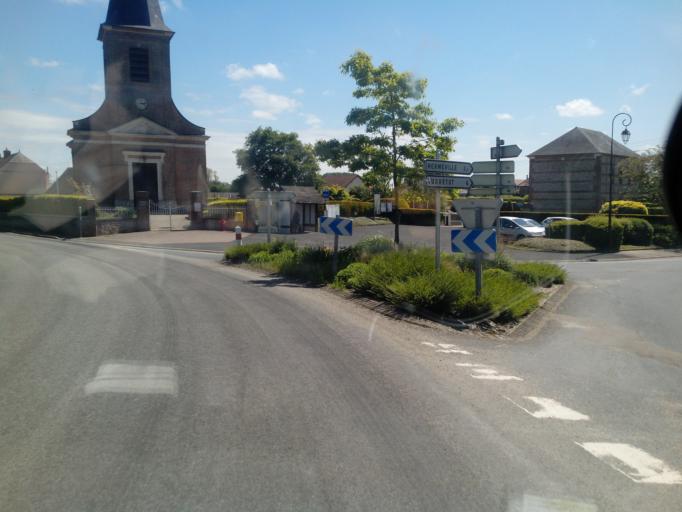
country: FR
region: Haute-Normandie
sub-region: Departement de la Seine-Maritime
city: Turretot
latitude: 49.6198
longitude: 0.2805
